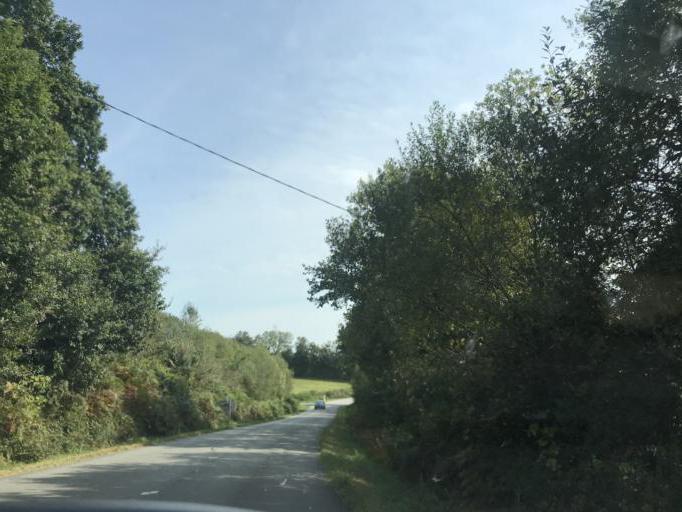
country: FR
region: Brittany
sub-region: Departement du Finistere
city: Loperec
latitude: 48.2963
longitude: -4.0665
